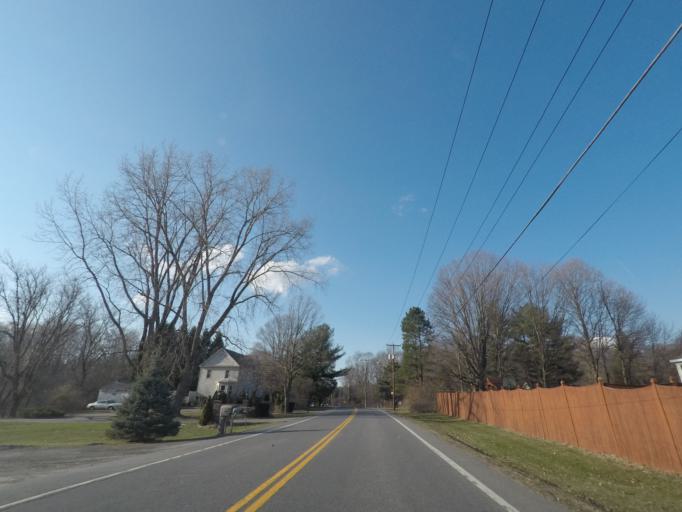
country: US
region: New York
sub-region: Schenectady County
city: Niskayuna
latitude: 42.8298
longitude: -73.7897
